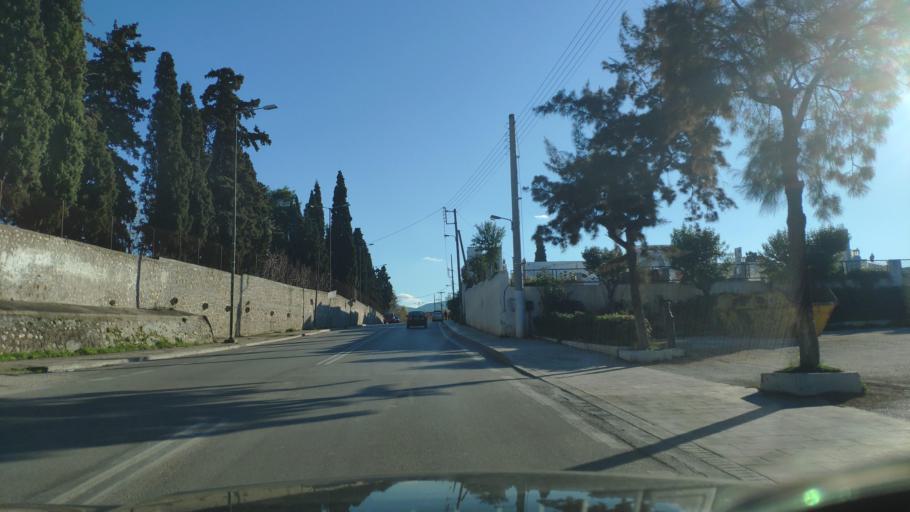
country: GR
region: Peloponnese
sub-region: Nomos Korinthias
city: Korinthos
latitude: 37.9320
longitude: 22.9282
